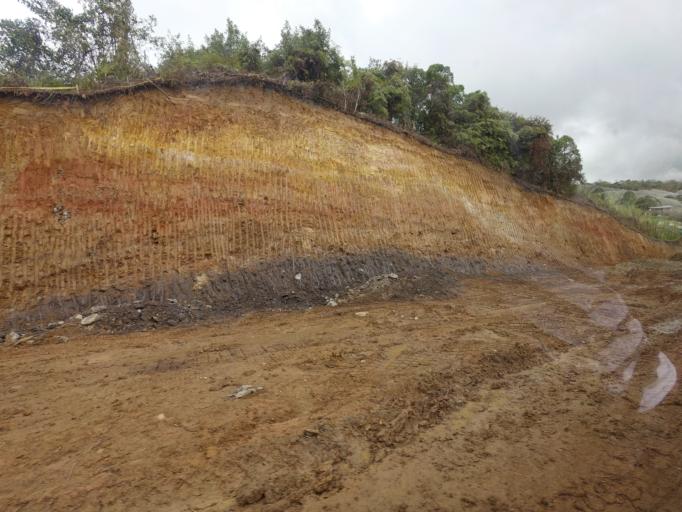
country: CO
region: Huila
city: San Agustin
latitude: 1.9520
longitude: -76.2965
